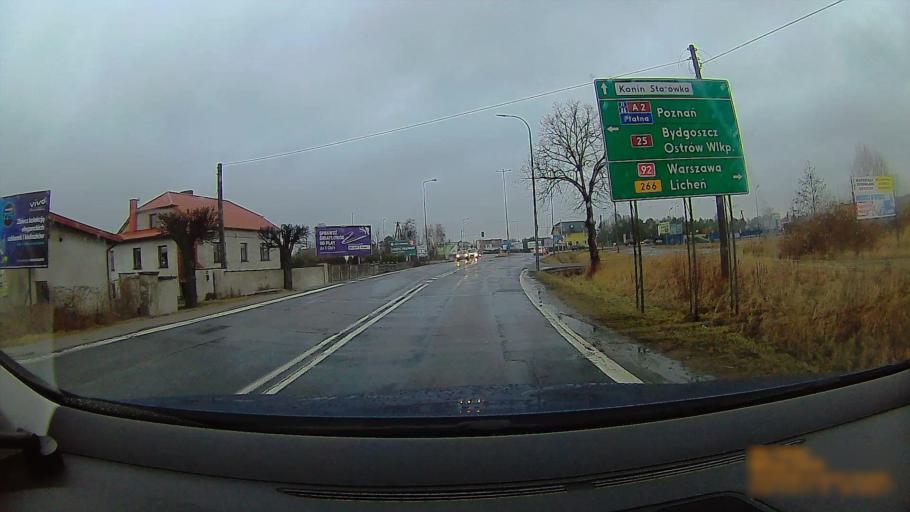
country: PL
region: Greater Poland Voivodeship
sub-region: Konin
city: Konin
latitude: 52.1908
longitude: 18.2644
